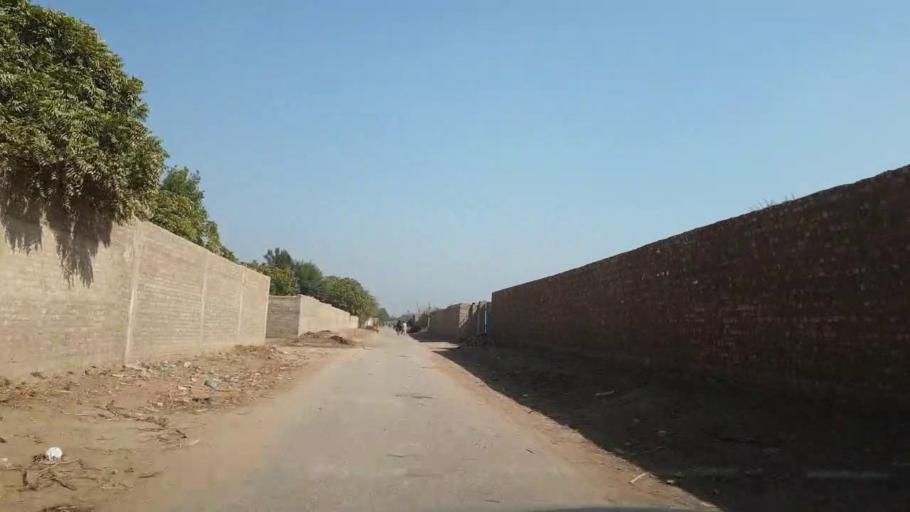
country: PK
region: Sindh
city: Tando Allahyar
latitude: 25.5645
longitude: 68.7027
